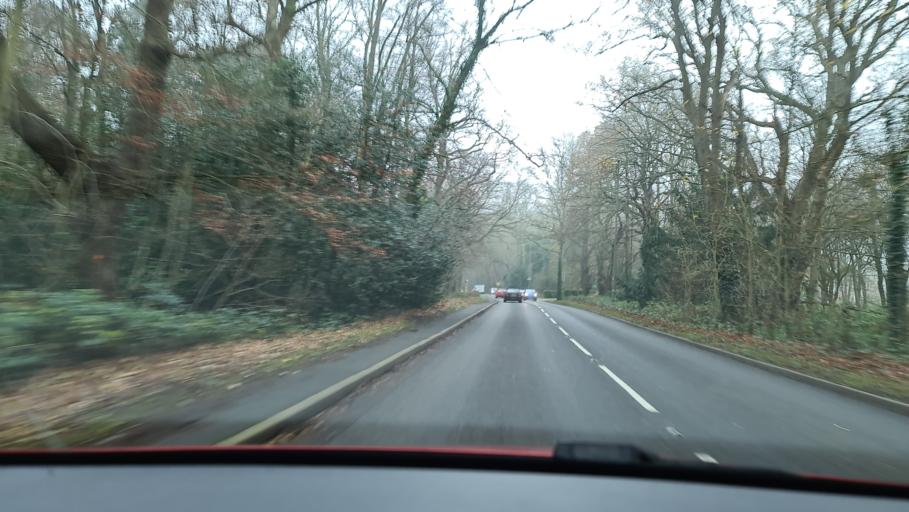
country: GB
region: England
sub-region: Surrey
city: Esher
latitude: 51.3573
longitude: -0.3626
